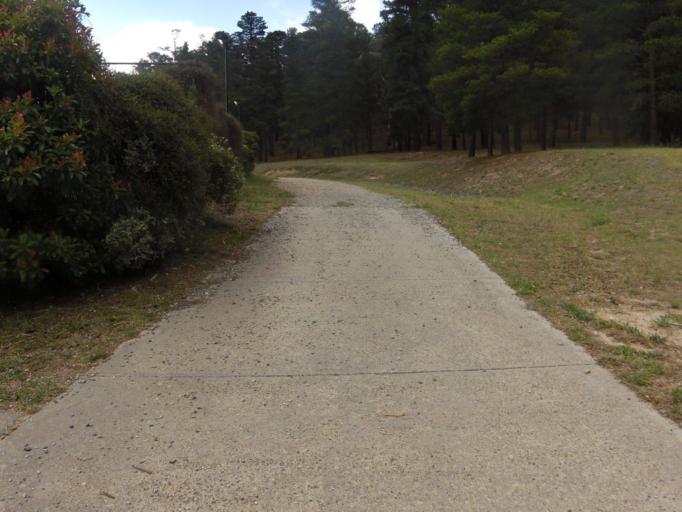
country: AU
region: Australian Capital Territory
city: Macarthur
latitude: -35.3691
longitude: 149.1163
